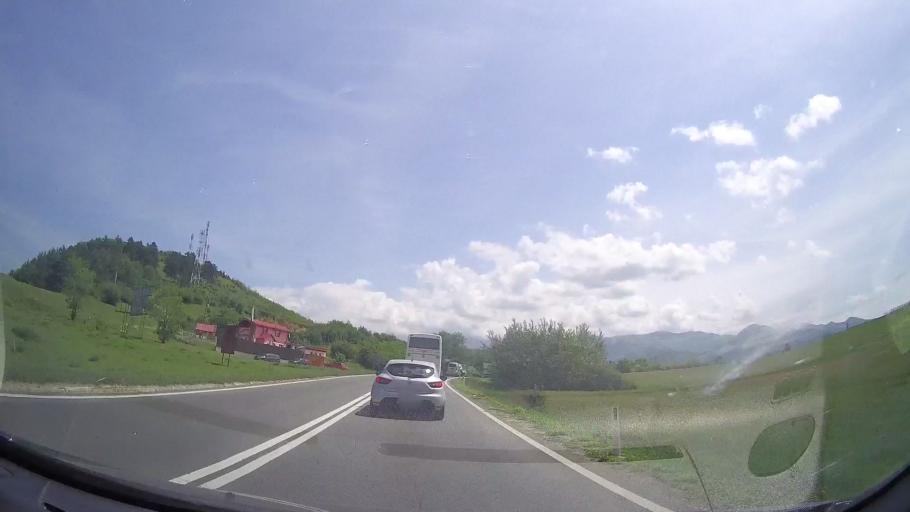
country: RO
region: Sibiu
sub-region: Comuna Talmaciu
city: Talmaciu
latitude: 45.6525
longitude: 24.2653
